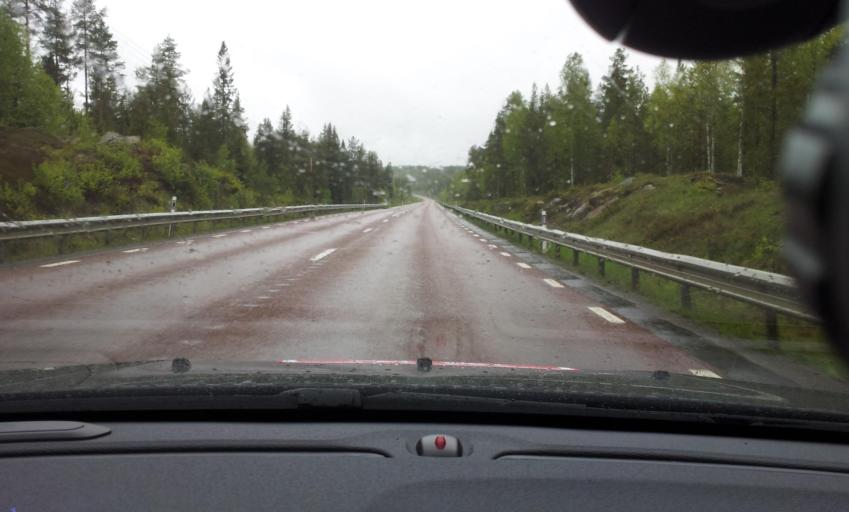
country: SE
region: Jaemtland
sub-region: Bergs Kommun
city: Hoverberg
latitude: 62.8646
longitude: 14.5190
